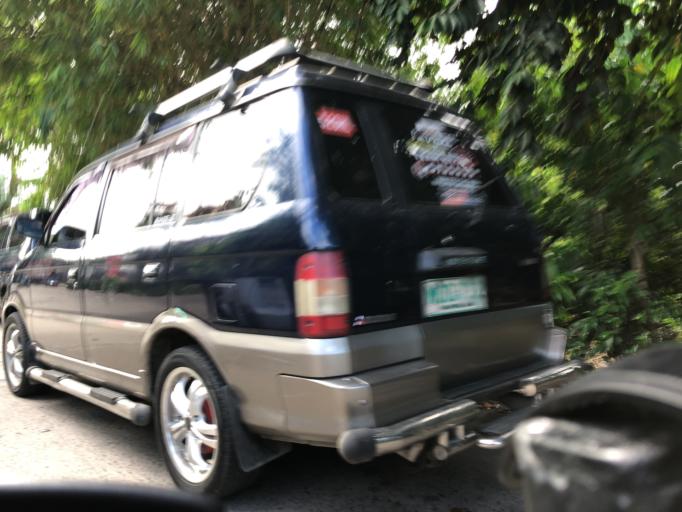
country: PH
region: Central Luzon
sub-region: Province of Bulacan
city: San Jose del Monte
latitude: 14.7591
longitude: 121.0510
